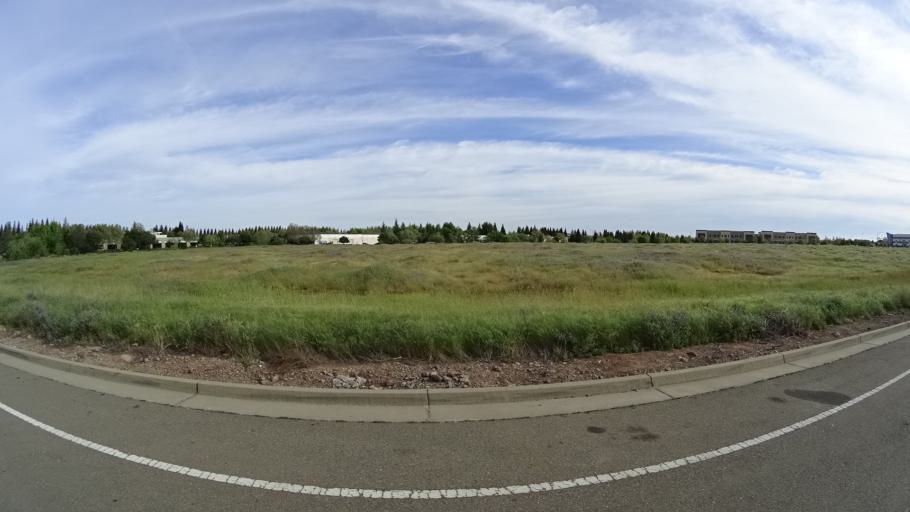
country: US
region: California
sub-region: Placer County
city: Roseville
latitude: 38.8100
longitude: -121.2951
